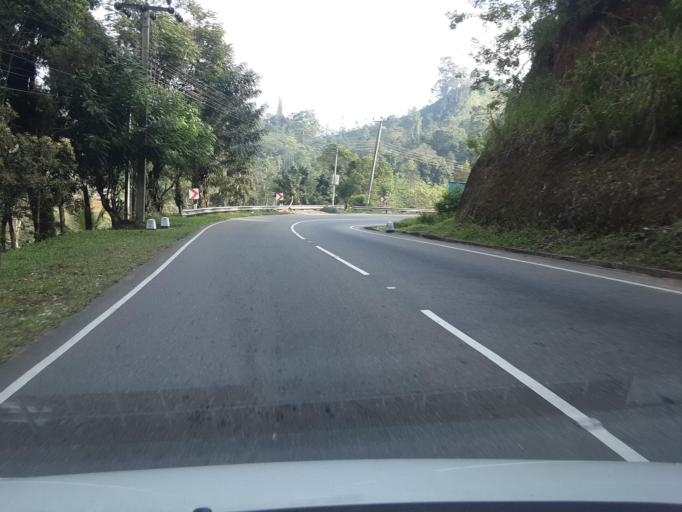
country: LK
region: Uva
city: Badulla
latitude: 6.9387
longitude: 80.9997
